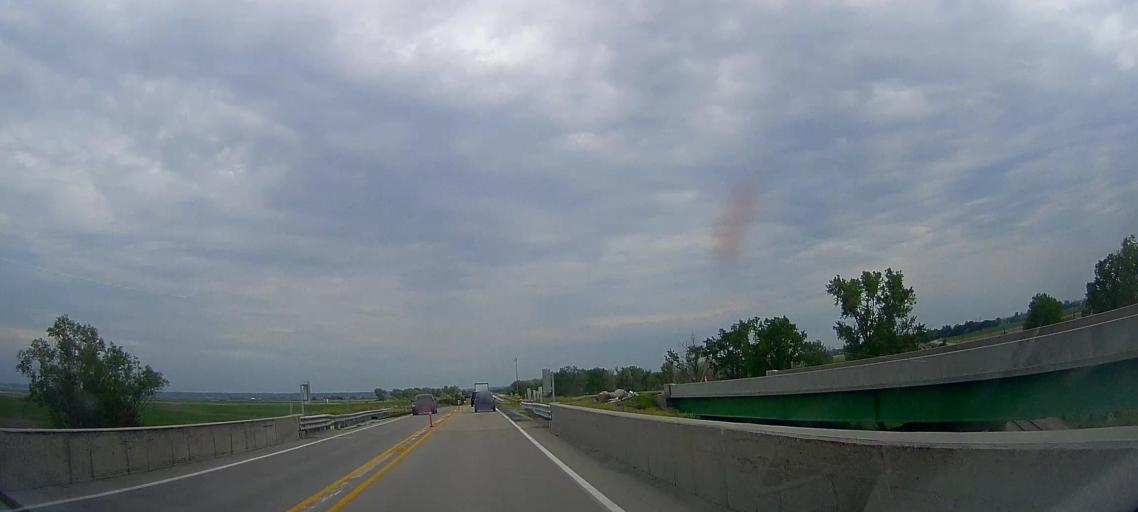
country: US
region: Nebraska
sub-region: Washington County
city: Blair
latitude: 41.6396
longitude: -96.0125
